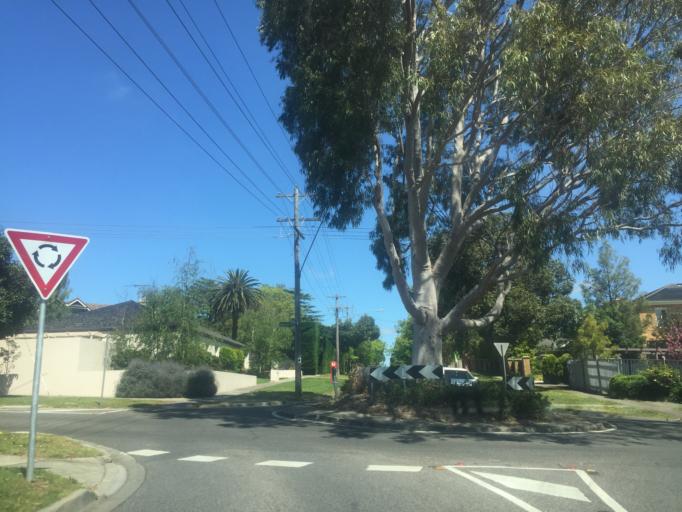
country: AU
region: Victoria
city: Mont Albert
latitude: -37.8081
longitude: 145.0962
